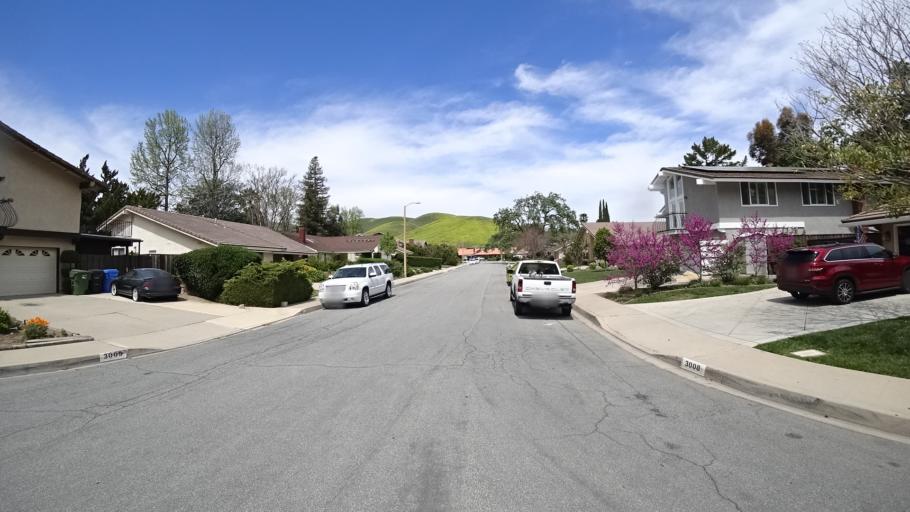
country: US
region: California
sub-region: Ventura County
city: Thousand Oaks
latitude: 34.1689
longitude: -118.8235
